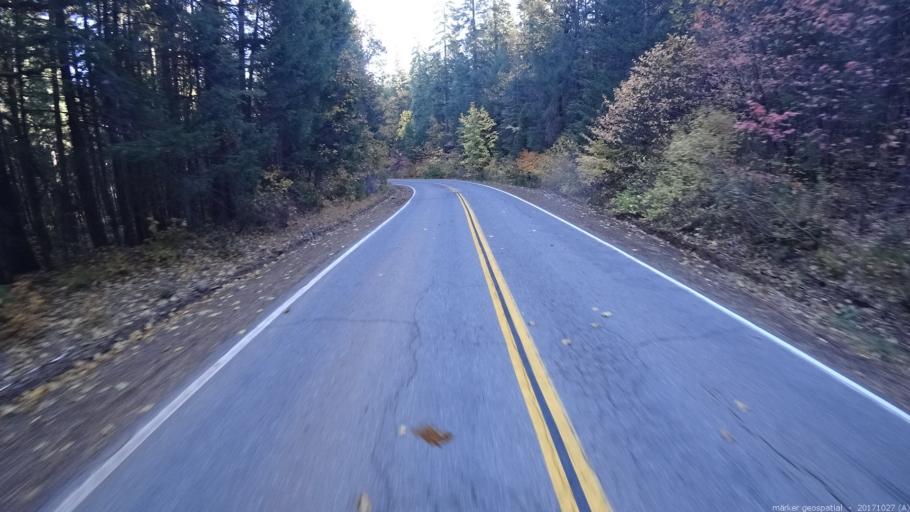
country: US
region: California
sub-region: Shasta County
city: Burney
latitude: 40.9828
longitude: -121.9289
